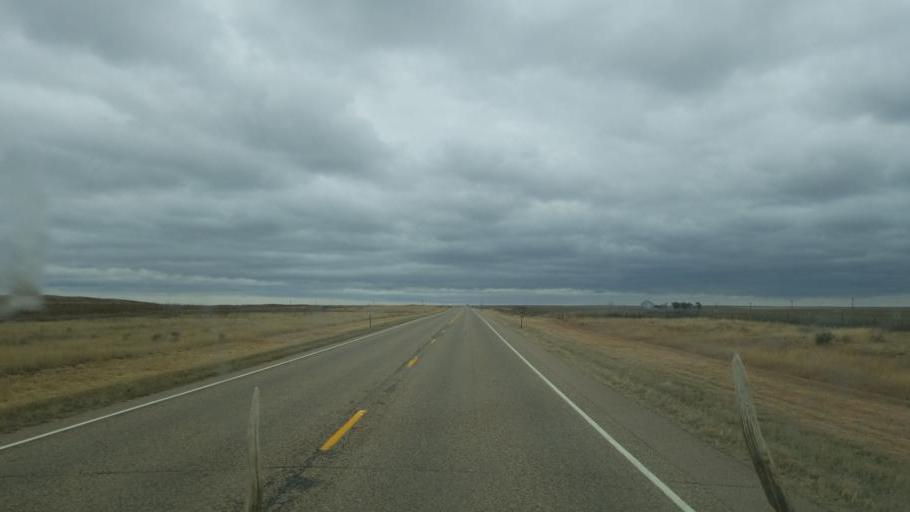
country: US
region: Colorado
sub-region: Cheyenne County
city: Cheyenne Wells
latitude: 38.7942
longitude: -102.6562
